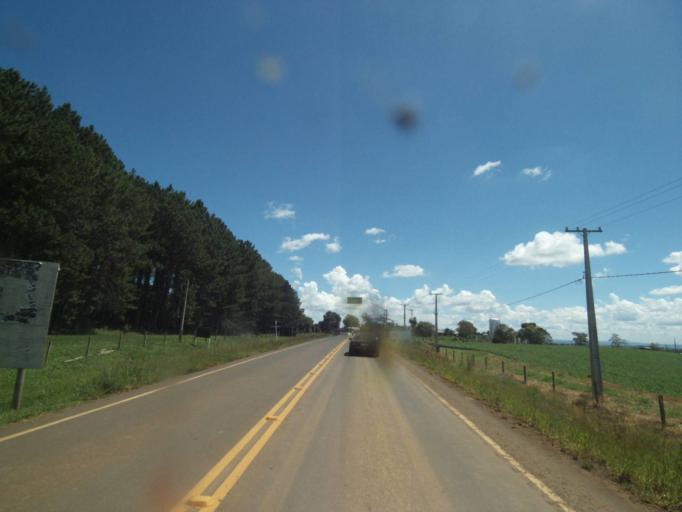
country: BR
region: Parana
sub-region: Pinhao
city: Pinhao
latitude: -25.8339
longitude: -52.0221
